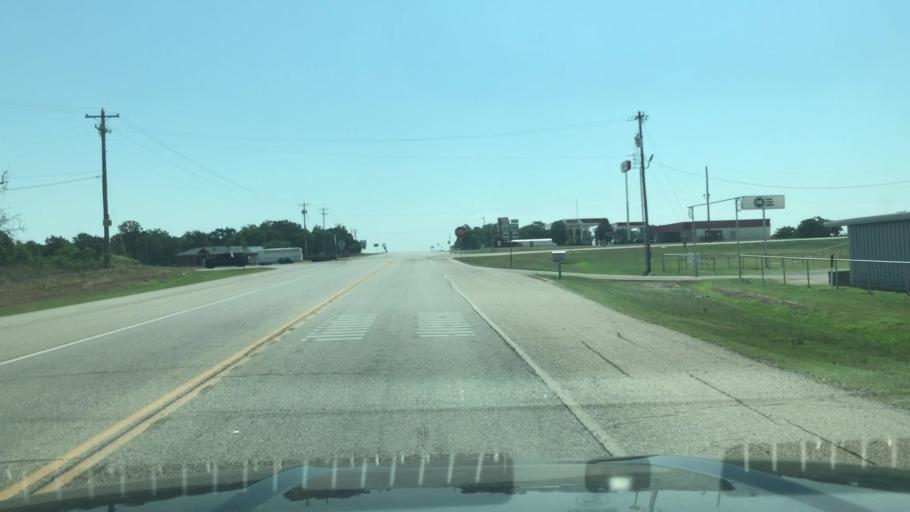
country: US
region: Oklahoma
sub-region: Creek County
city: Mannford
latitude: 36.0031
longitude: -96.3884
